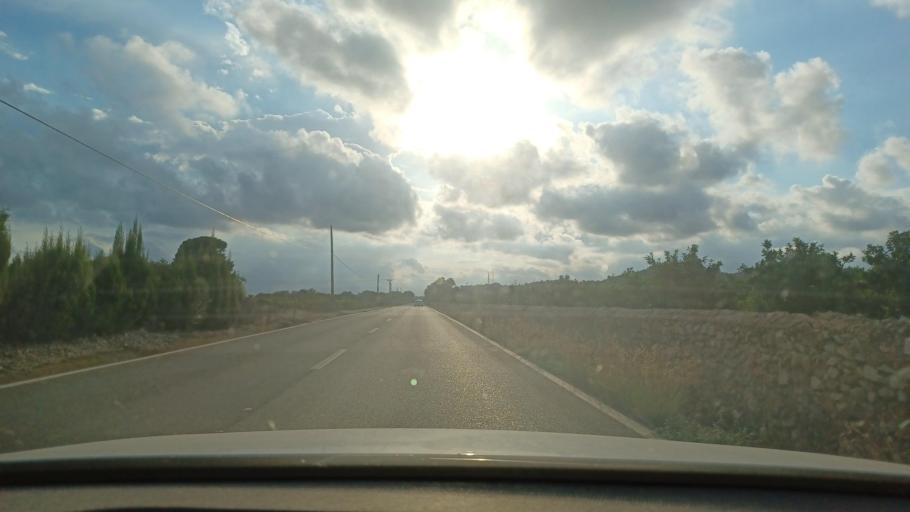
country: ES
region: Catalonia
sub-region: Provincia de Tarragona
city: Alcanar
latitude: 40.5469
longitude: 0.5037
